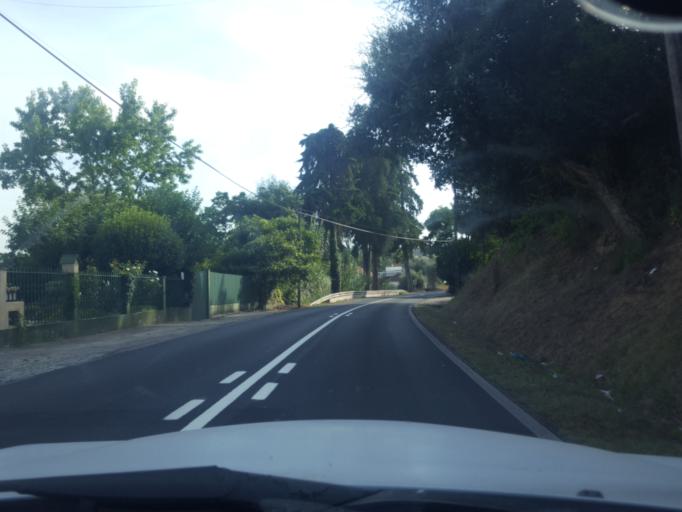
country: PT
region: Leiria
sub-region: Leiria
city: Leiria
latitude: 39.7126
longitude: -8.7891
